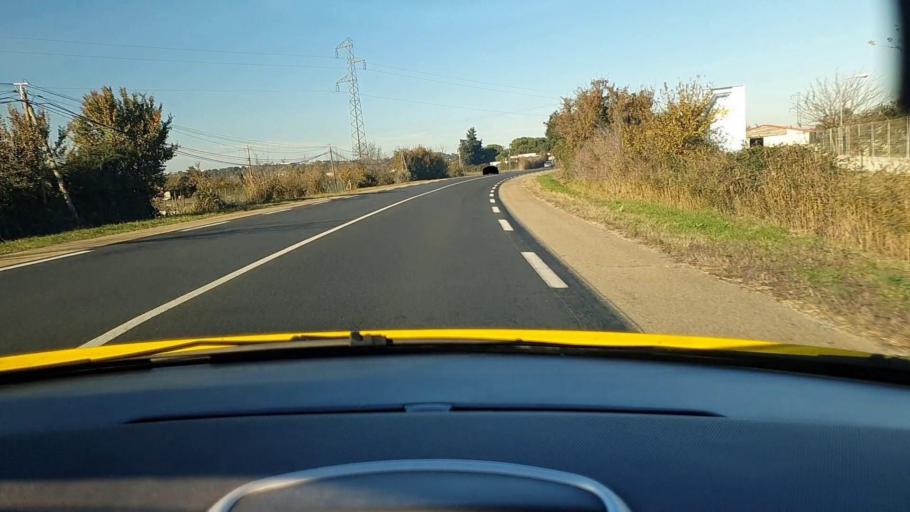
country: FR
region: Languedoc-Roussillon
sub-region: Departement du Gard
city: Bellegarde
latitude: 43.7347
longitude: 4.5228
